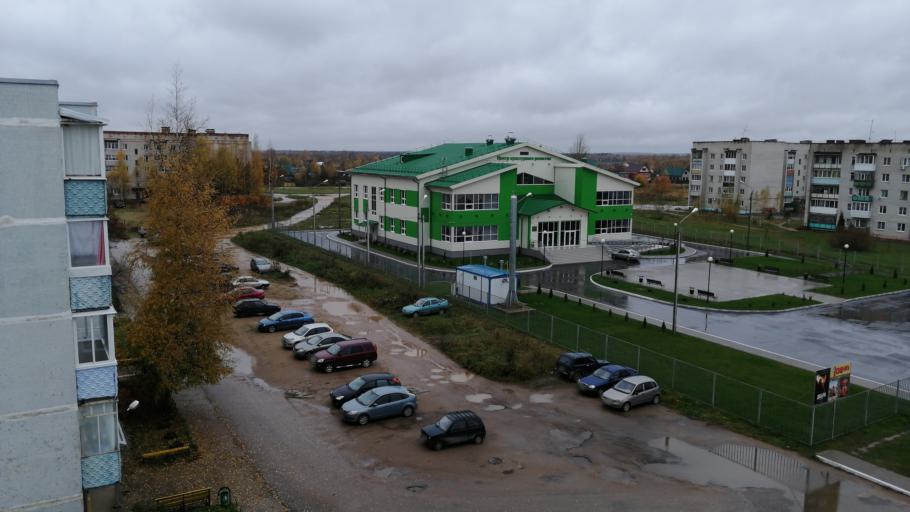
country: RU
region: Smolensk
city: Ozernyy
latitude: 55.5738
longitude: 32.4062
